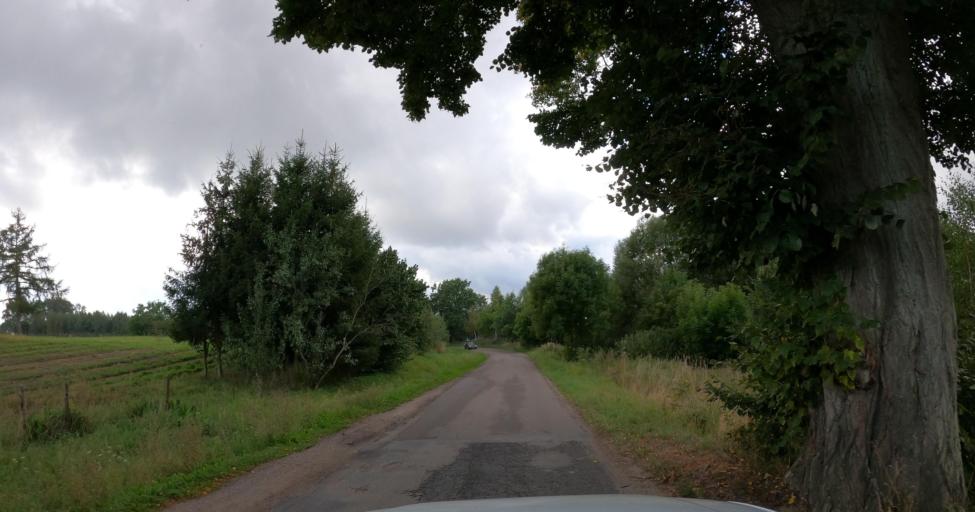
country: PL
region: West Pomeranian Voivodeship
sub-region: Powiat kolobrzeski
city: Goscino
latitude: 54.0782
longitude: 15.6098
